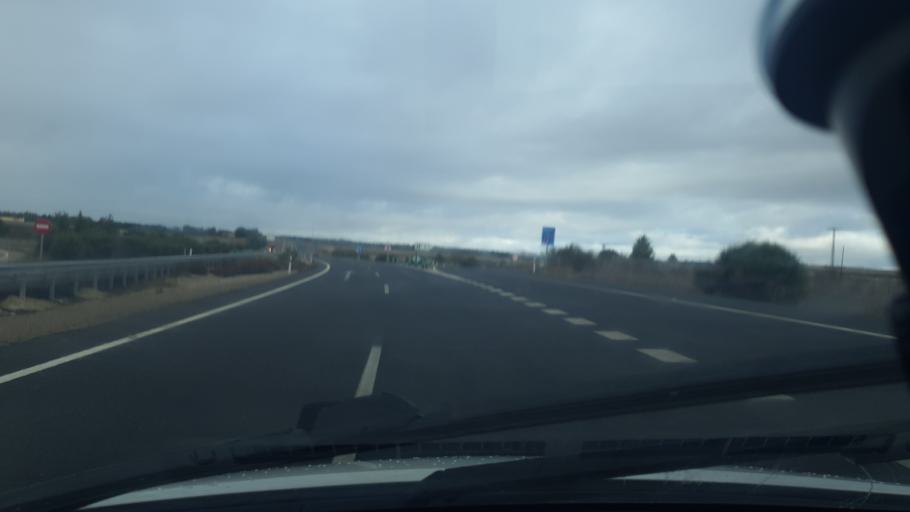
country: ES
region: Castille and Leon
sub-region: Provincia de Segovia
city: Cuellar
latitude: 41.4051
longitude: -4.2943
